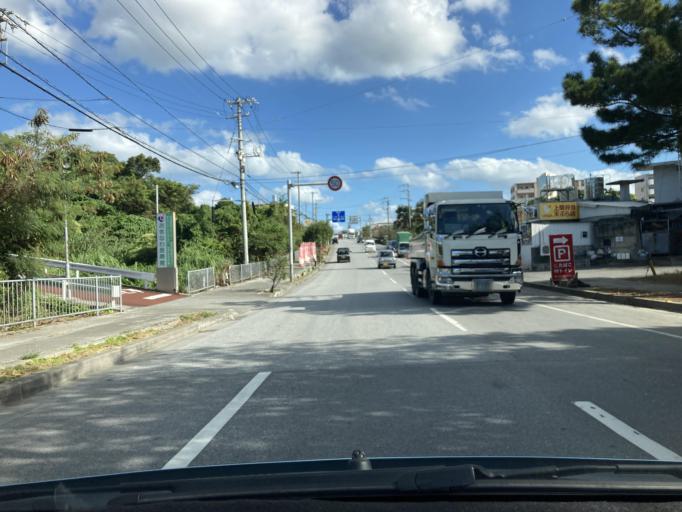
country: JP
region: Okinawa
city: Okinawa
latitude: 26.3743
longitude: 127.8227
